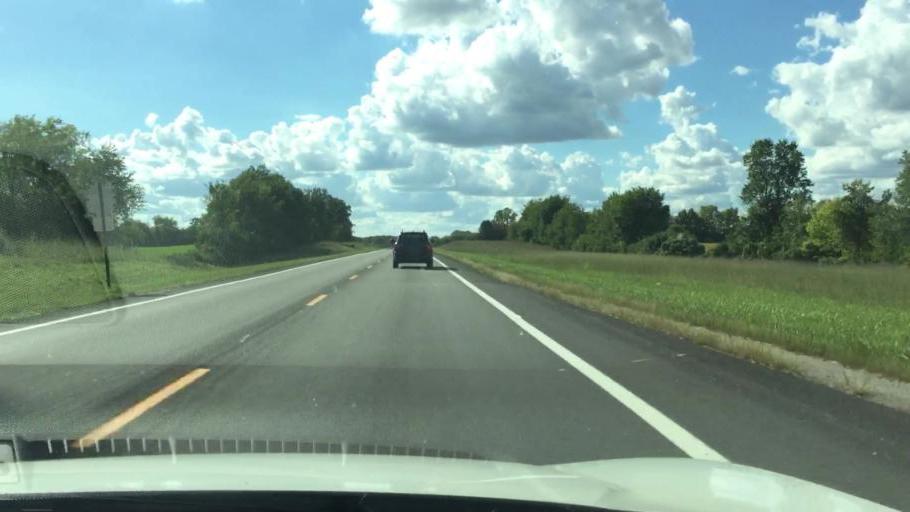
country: US
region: Ohio
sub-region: Clark County
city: Northridge
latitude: 39.9770
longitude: -83.7562
